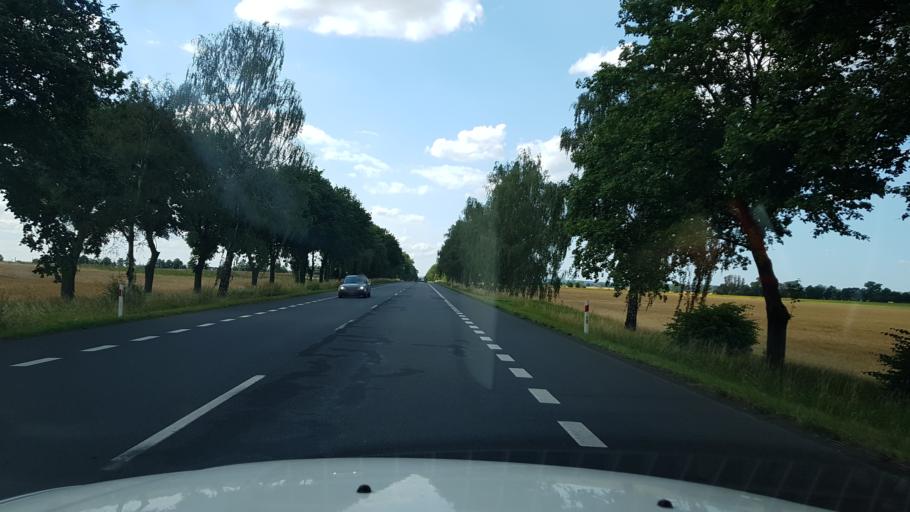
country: PL
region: West Pomeranian Voivodeship
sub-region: Powiat gryfinski
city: Stare Czarnowo
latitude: 53.2060
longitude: 14.8133
